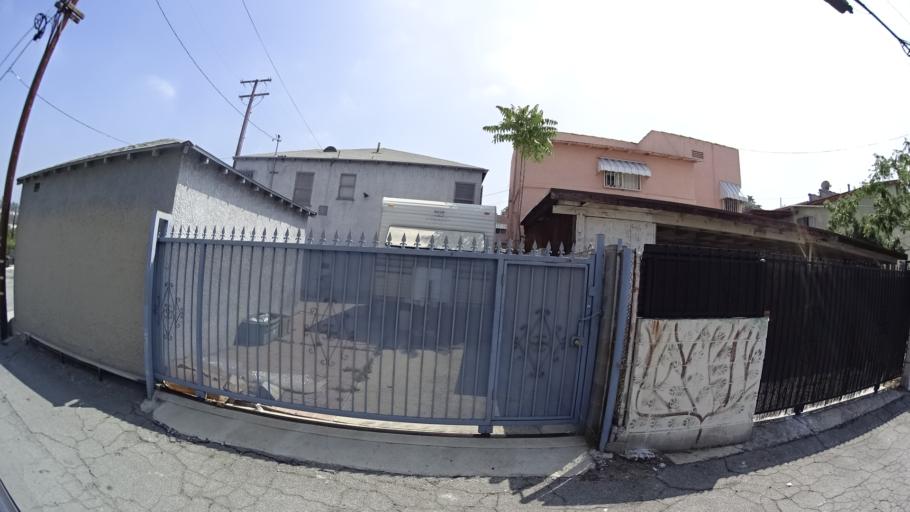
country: US
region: California
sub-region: Los Angeles County
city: Belvedere
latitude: 34.0596
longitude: -118.1724
